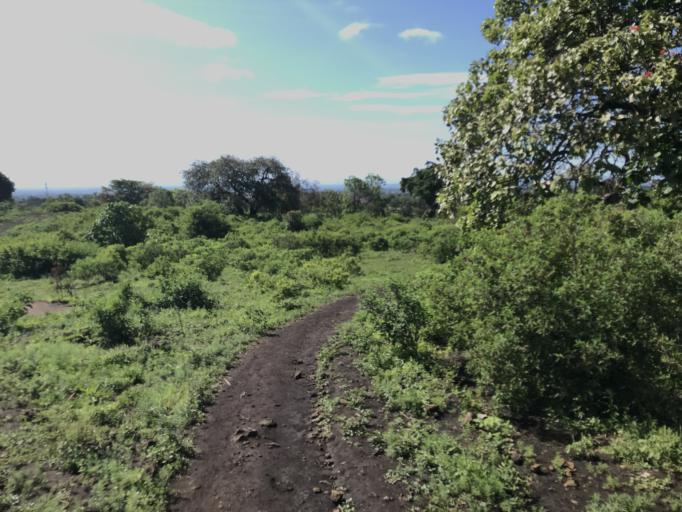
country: TZ
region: Arusha
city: Usa River
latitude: -3.3936
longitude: 36.7973
